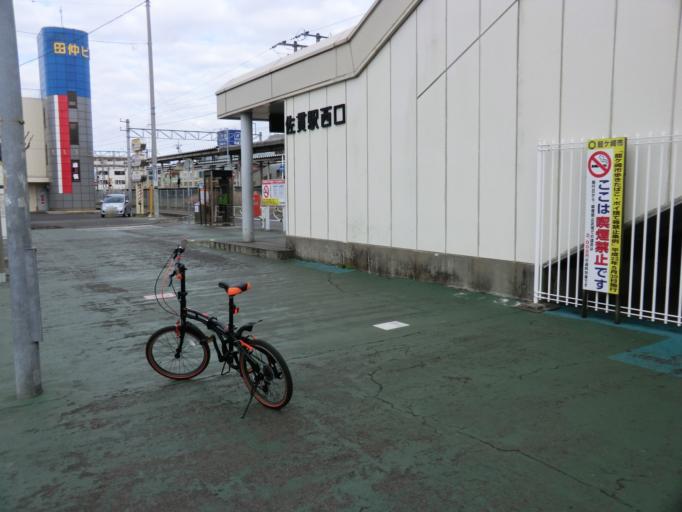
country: JP
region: Ibaraki
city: Fujishiro
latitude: 35.9306
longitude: 140.1379
